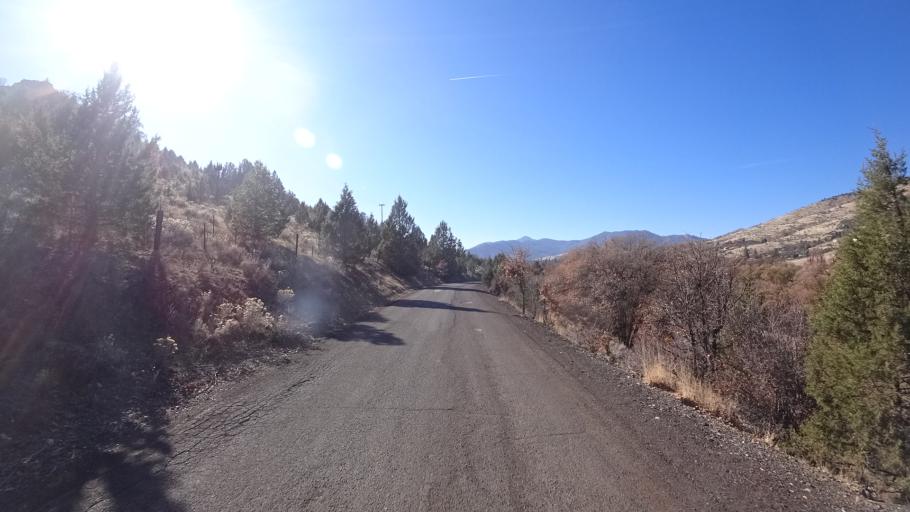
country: US
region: California
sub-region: Siskiyou County
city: Yreka
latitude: 41.7728
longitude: -122.5980
